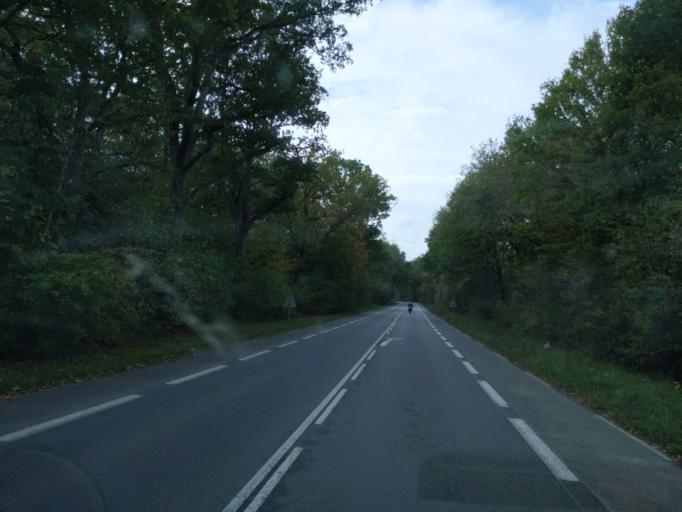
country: FR
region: Ile-de-France
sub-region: Departement des Yvelines
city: Auffargis
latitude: 48.6532
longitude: 1.8830
